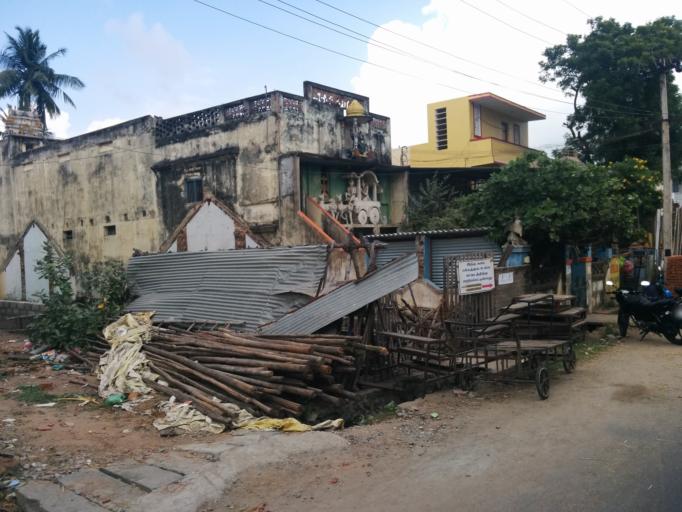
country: IN
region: Tamil Nadu
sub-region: Kancheepuram
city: Madurantakam
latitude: 12.5102
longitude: 79.8879
